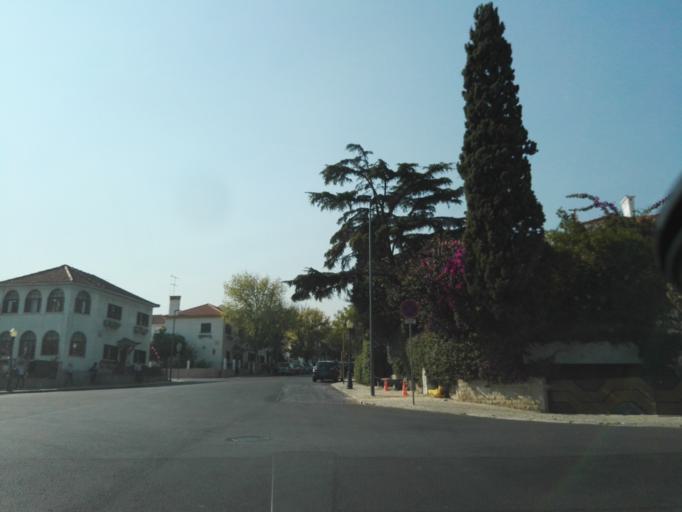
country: PT
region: Lisbon
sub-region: Lisbon
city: Lisbon
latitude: 38.7314
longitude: -9.1112
